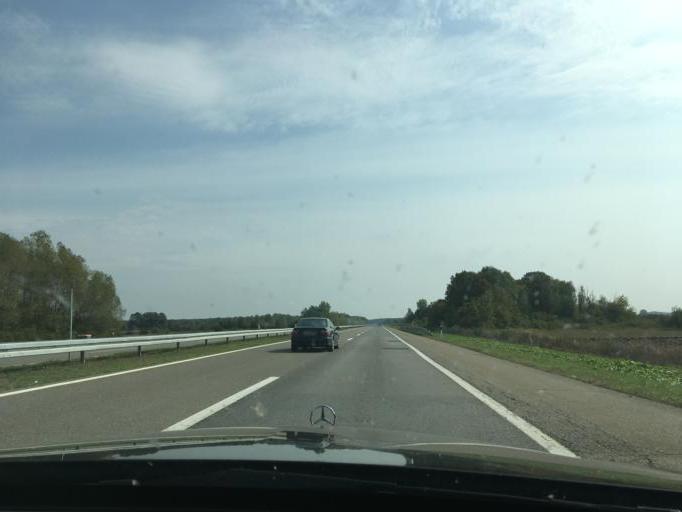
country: HR
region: Vukovarsko-Srijemska
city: Stitar
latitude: 45.1116
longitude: 18.5836
